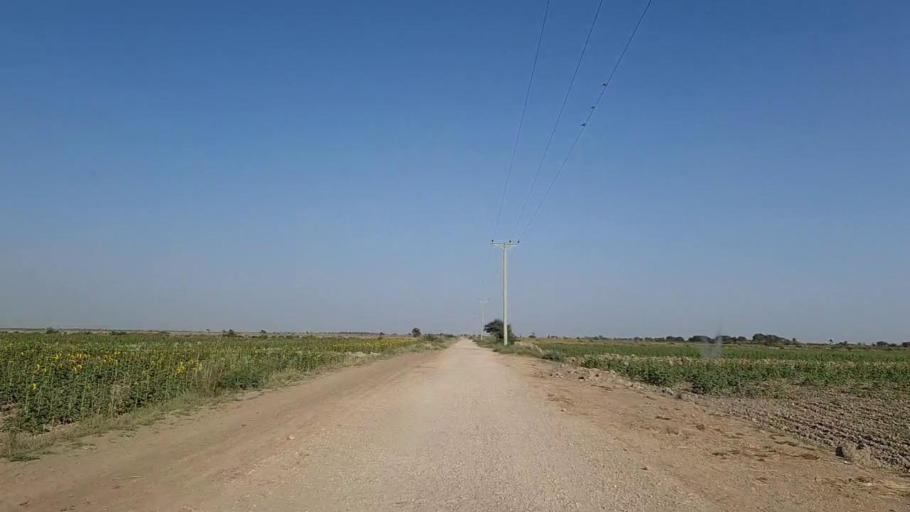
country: PK
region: Sindh
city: Jati
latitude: 24.4233
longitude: 68.2656
